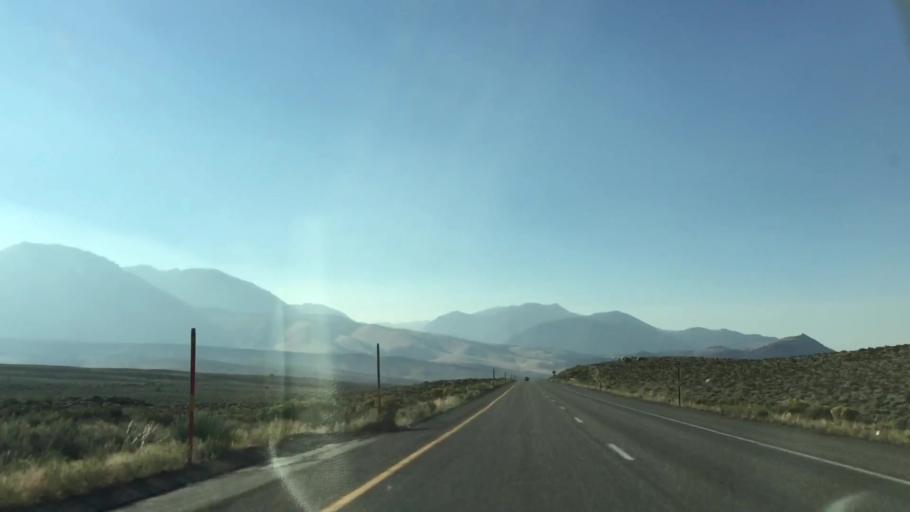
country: US
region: California
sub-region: Mono County
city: Mammoth Lakes
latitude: 37.8450
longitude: -119.0745
